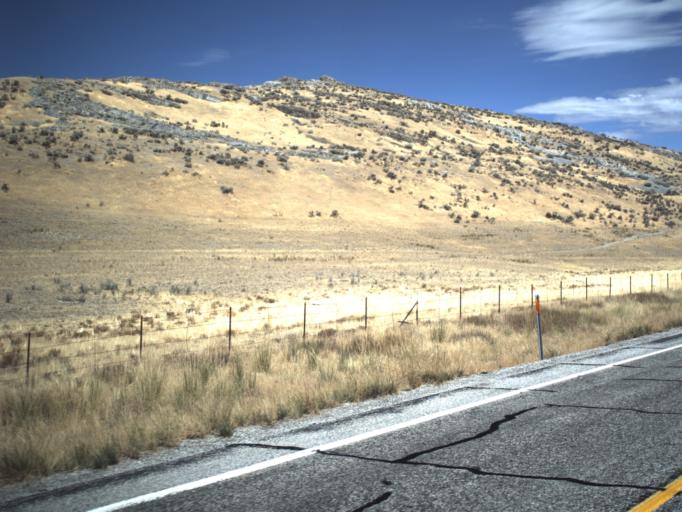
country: US
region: Utah
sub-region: Box Elder County
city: Tremonton
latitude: 41.6742
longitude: -112.4462
